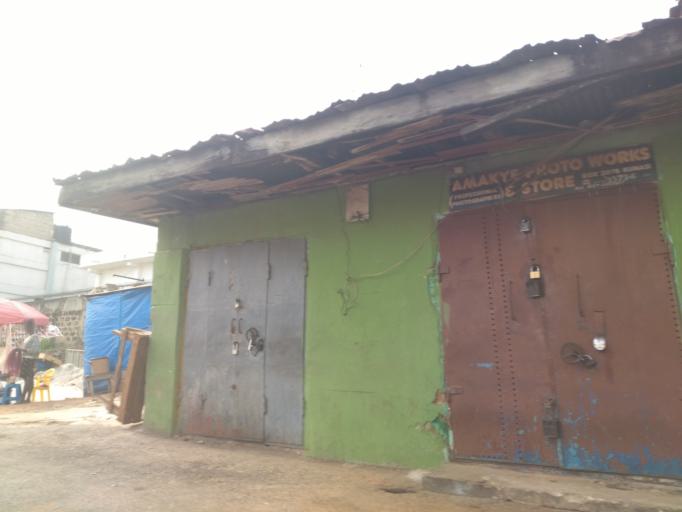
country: GH
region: Ashanti
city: Kumasi
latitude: 6.6901
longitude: -1.6211
